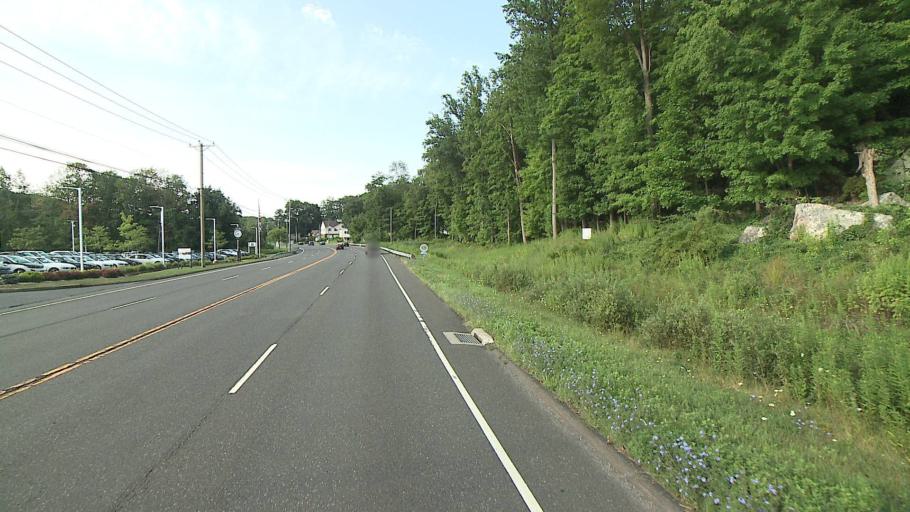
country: US
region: Connecticut
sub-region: Fairfield County
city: Ridgefield
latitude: 41.3309
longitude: -73.4731
